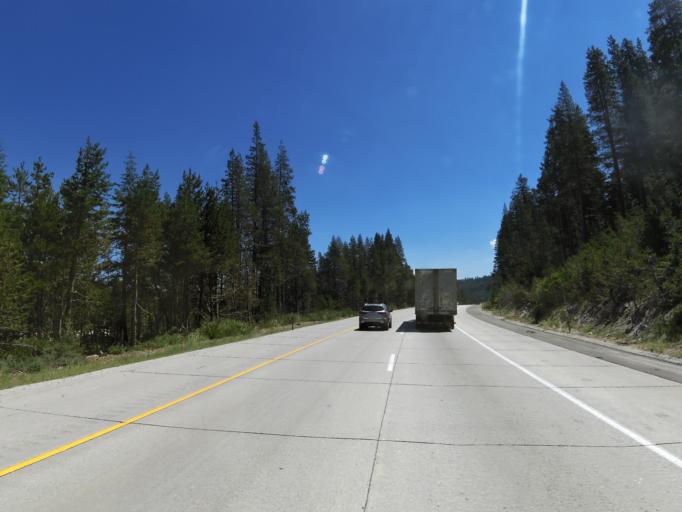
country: US
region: California
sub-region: Nevada County
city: Truckee
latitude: 39.3152
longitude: -120.4615
